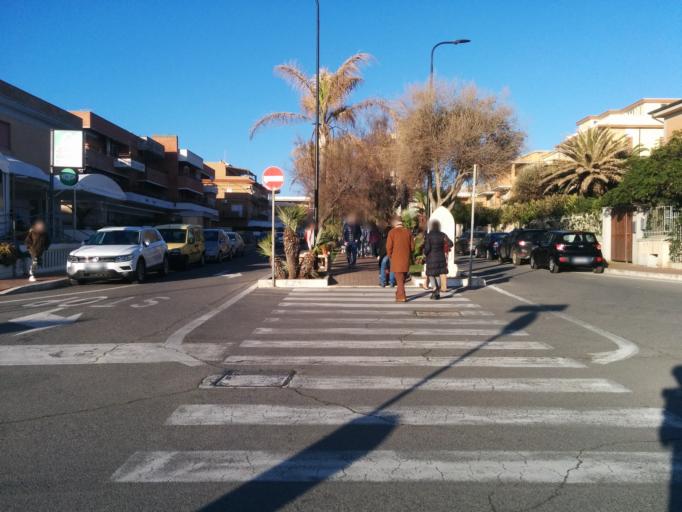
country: IT
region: Latium
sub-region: Citta metropolitana di Roma Capitale
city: Lavinio
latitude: 41.4979
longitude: 12.5847
